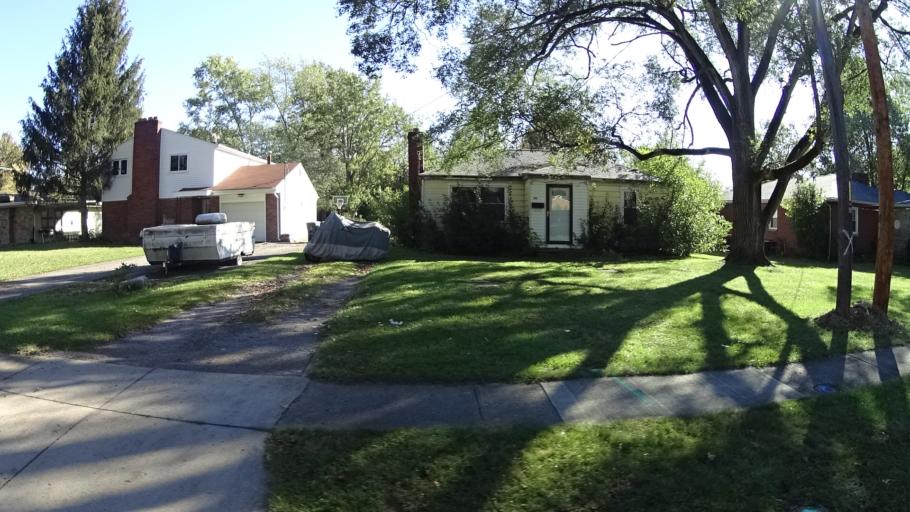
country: US
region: Ohio
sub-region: Lorain County
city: Oberlin
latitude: 41.2818
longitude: -82.2151
